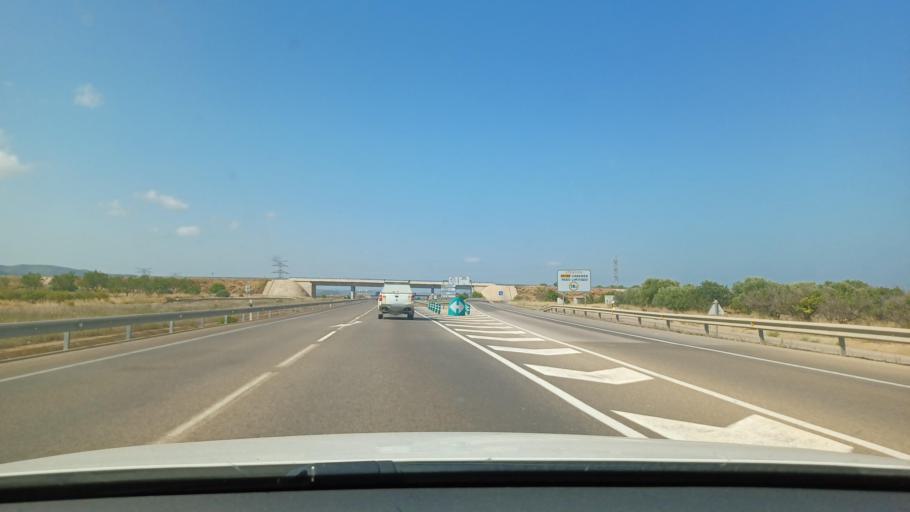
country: ES
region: Valencia
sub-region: Provincia de Castello
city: Orpesa/Oropesa del Mar
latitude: 40.1199
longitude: 0.1424
